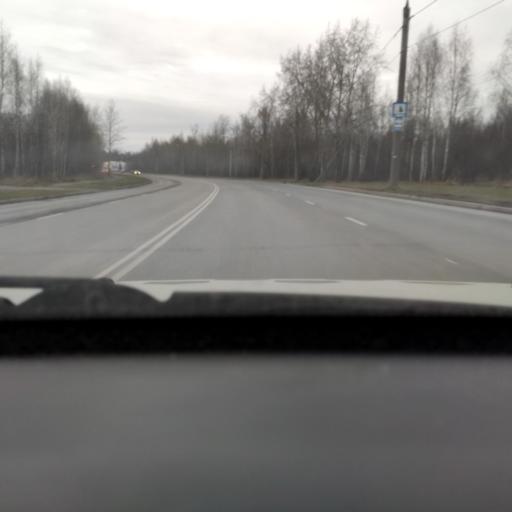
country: RU
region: Perm
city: Polazna
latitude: 58.1287
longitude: 56.4066
